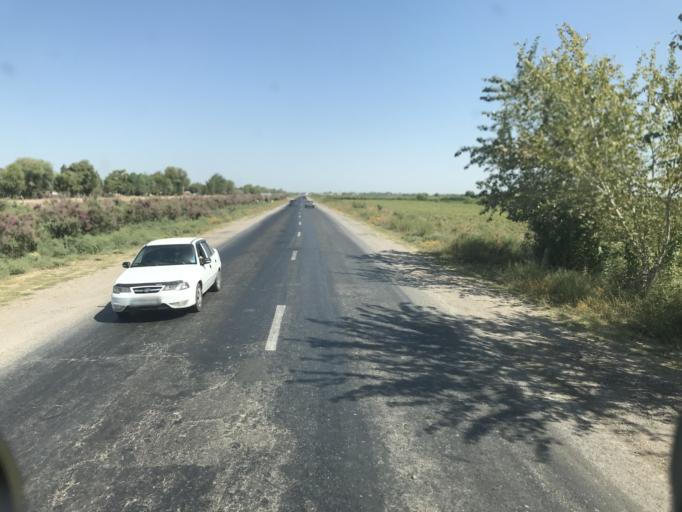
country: KZ
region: Ongtustik Qazaqstan
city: Ilyich
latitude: 40.7712
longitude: 68.5373
